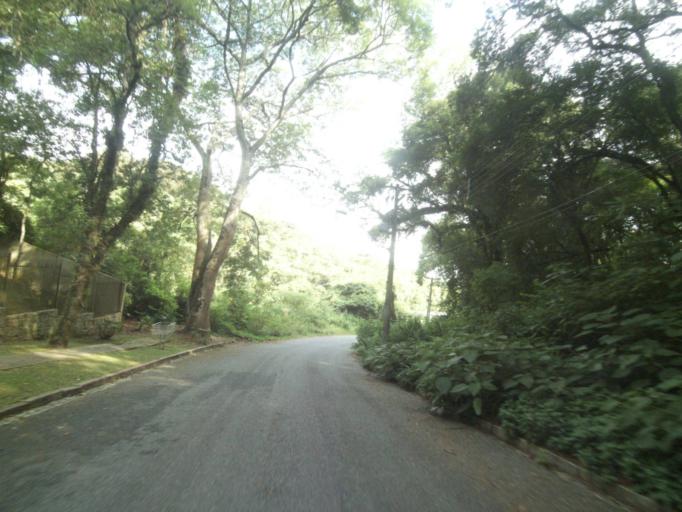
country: BR
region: Parana
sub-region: Curitiba
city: Curitiba
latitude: -25.4111
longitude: -49.3168
